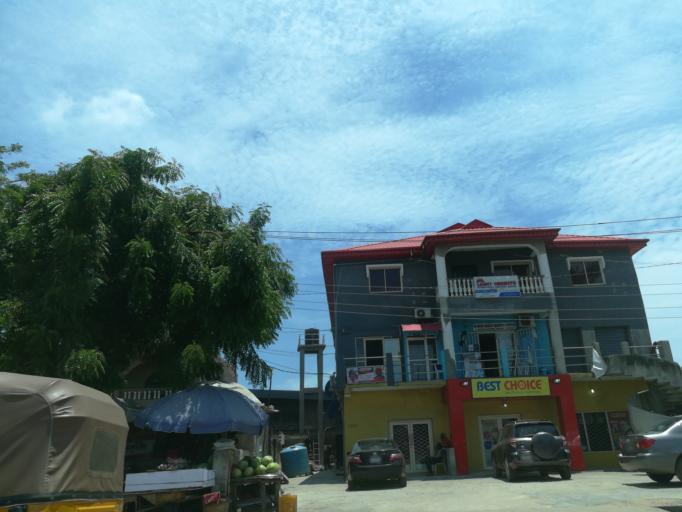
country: NG
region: Lagos
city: Ebute Ikorodu
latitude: 6.6039
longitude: 3.4931
